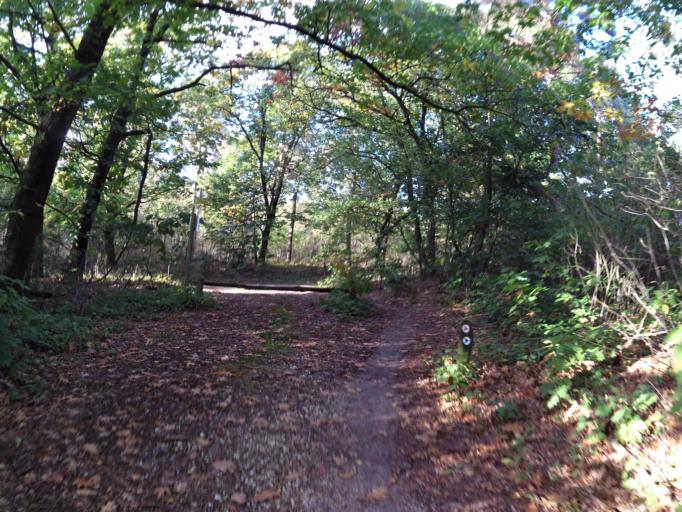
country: NL
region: Limburg
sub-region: Gemeente Bergen
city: Wellerlooi
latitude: 51.5590
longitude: 6.1204
